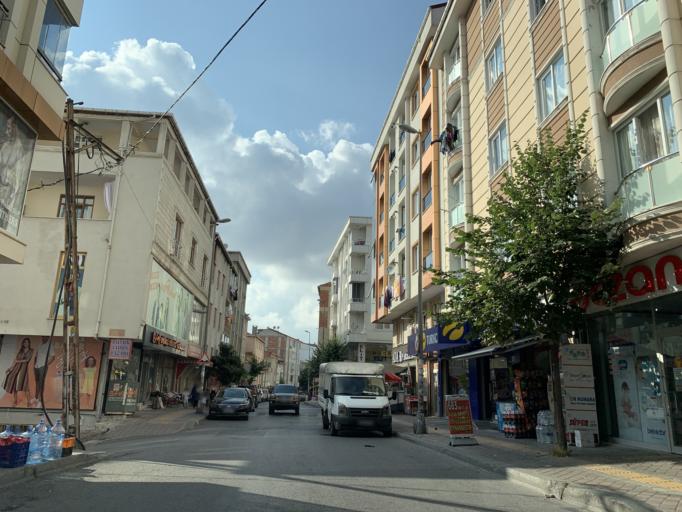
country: TR
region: Istanbul
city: Esenyurt
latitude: 41.0282
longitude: 28.6776
